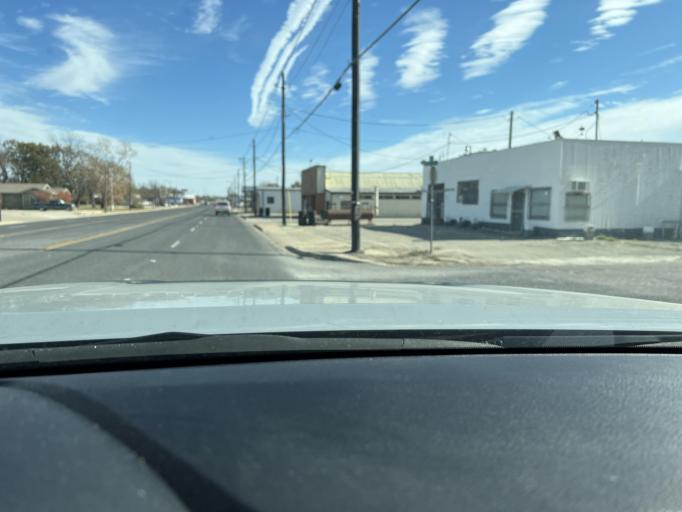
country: US
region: Texas
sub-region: Eastland County
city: Eastland
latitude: 32.4017
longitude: -98.8166
